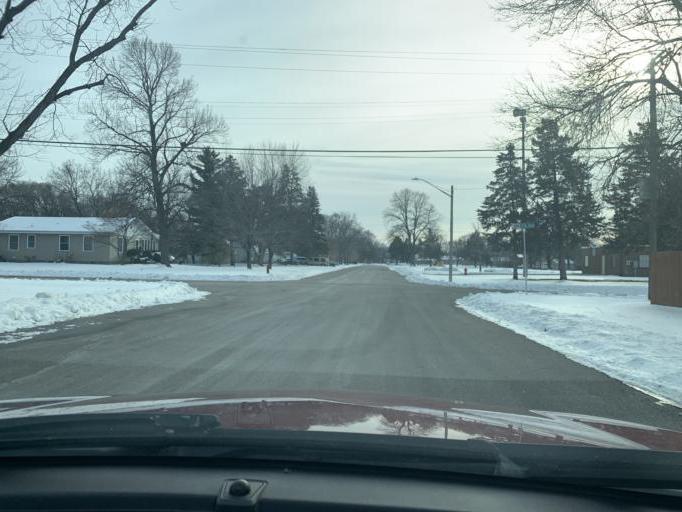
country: US
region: Minnesota
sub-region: Washington County
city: Saint Paul Park
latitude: 44.8389
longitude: -92.9886
